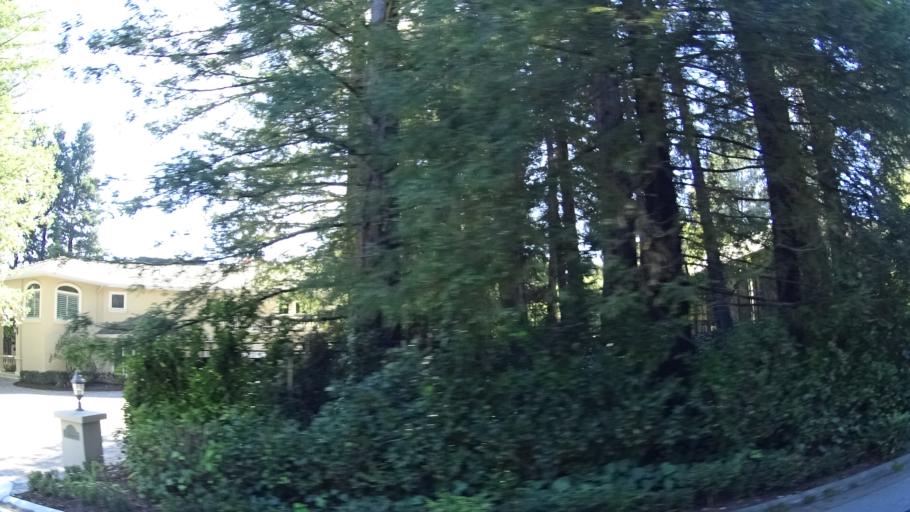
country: US
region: California
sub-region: San Mateo County
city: Burlingame
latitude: 37.5743
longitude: -122.3655
